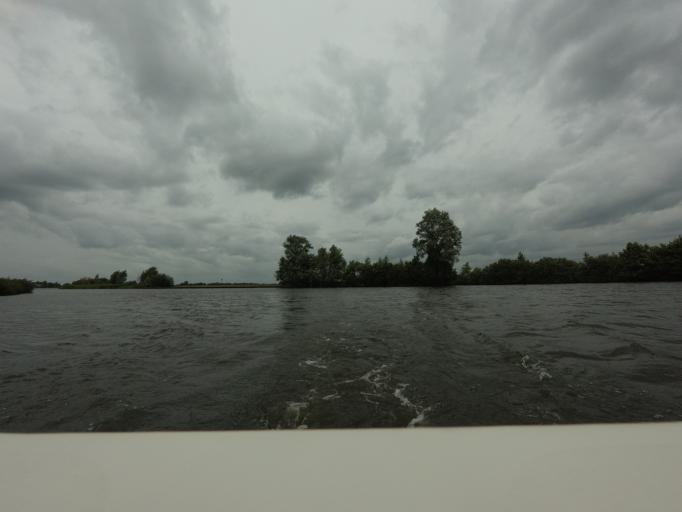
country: NL
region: Friesland
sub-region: Gemeente Boarnsterhim
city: Aldeboarn
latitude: 53.0981
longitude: 5.9191
